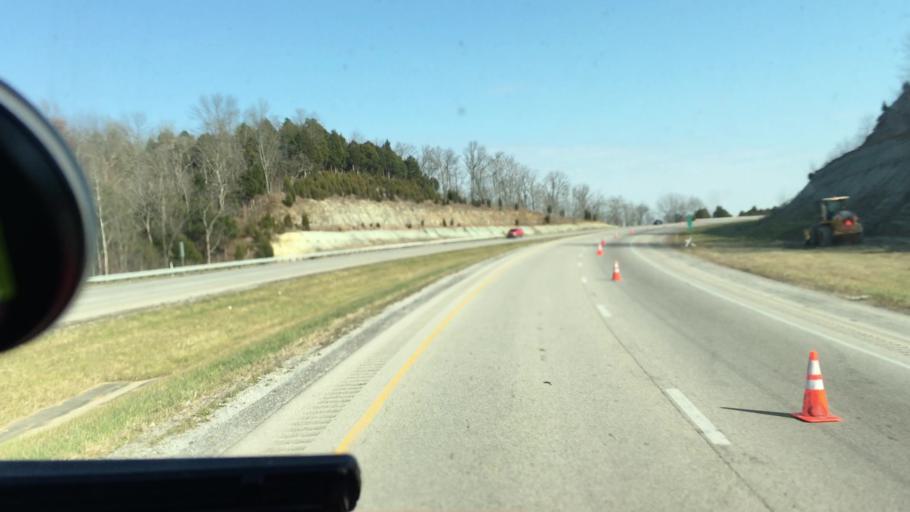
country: US
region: Kentucky
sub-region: Bath County
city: Owingsville
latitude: 38.1235
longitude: -83.7914
